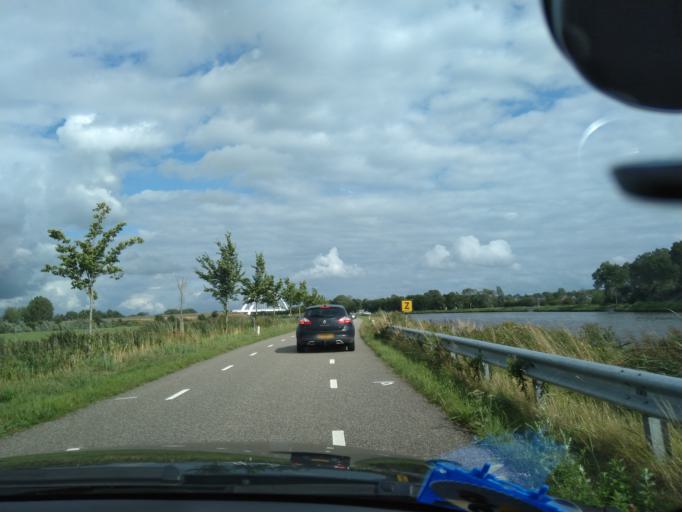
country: NL
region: Groningen
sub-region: Gemeente Zuidhorn
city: Noordhorn
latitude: 53.2536
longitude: 6.3805
